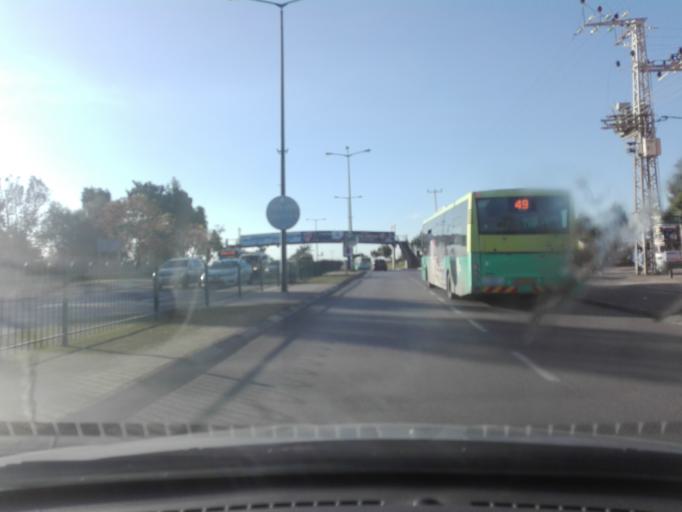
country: IL
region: Central District
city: Netanya
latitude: 32.3102
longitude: 34.8548
